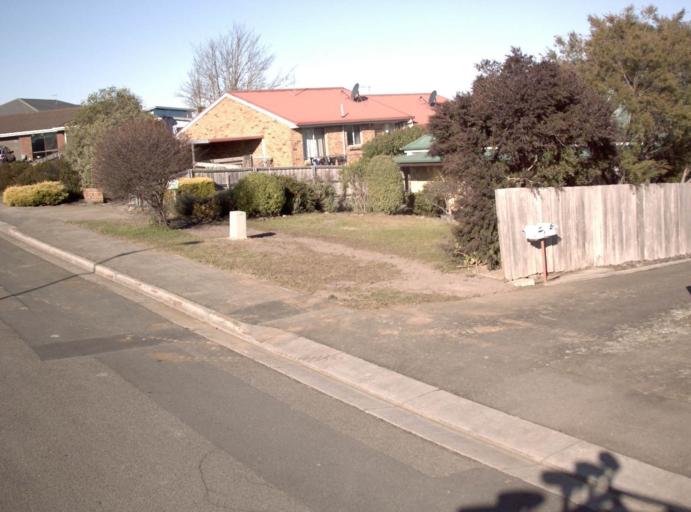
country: AU
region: Tasmania
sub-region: Launceston
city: Summerhill
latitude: -41.4624
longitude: 147.1276
